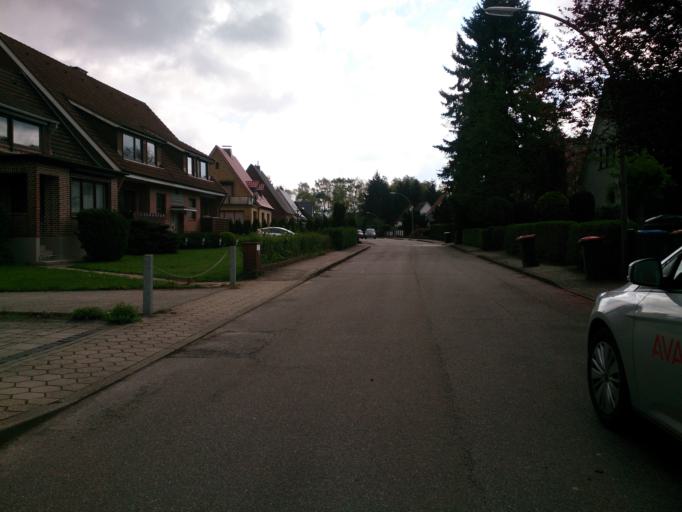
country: DE
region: Hamburg
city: Harburg
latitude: 53.4730
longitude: 9.9043
